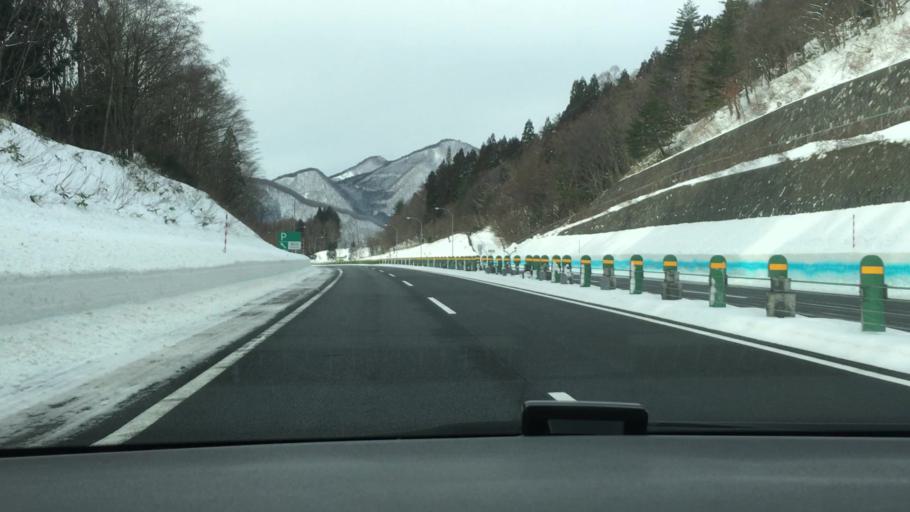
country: JP
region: Akita
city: Hanawa
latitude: 40.1370
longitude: 140.9662
